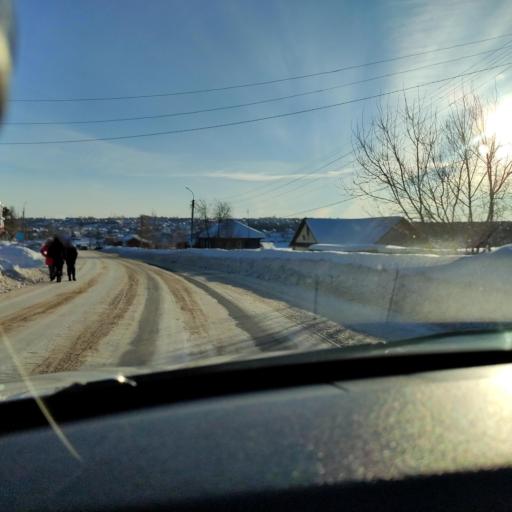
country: RU
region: Perm
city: Polazna
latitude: 58.3098
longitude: 56.4219
